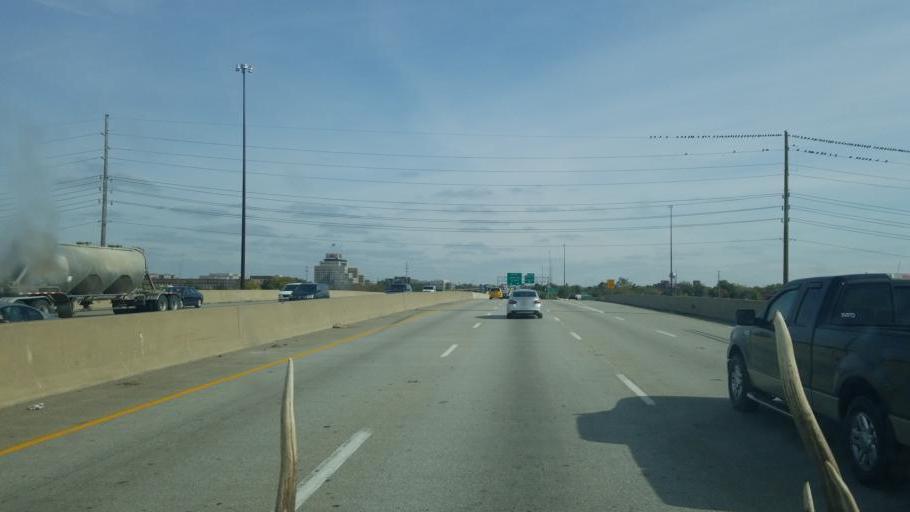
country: US
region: Indiana
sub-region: Marion County
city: Indianapolis
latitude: 39.7536
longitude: -86.1665
